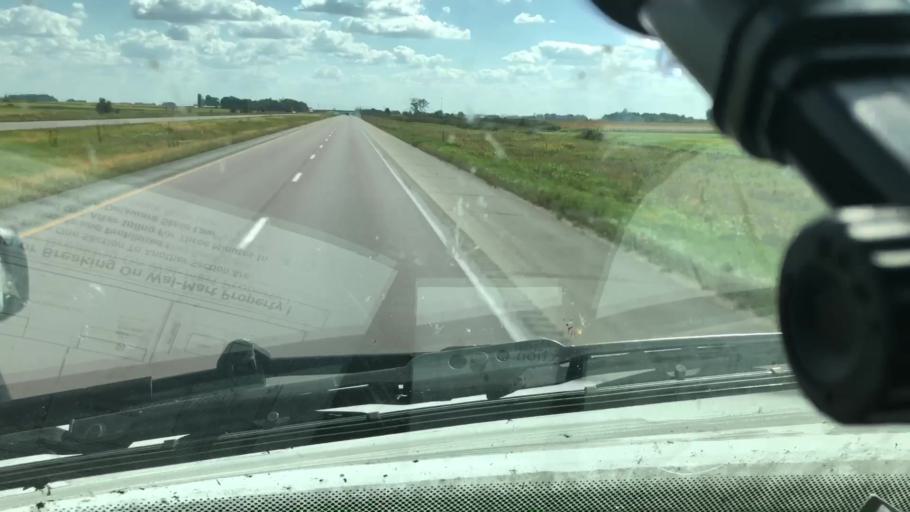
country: US
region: Iowa
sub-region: Worth County
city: Northwood
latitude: 43.3737
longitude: -93.3493
